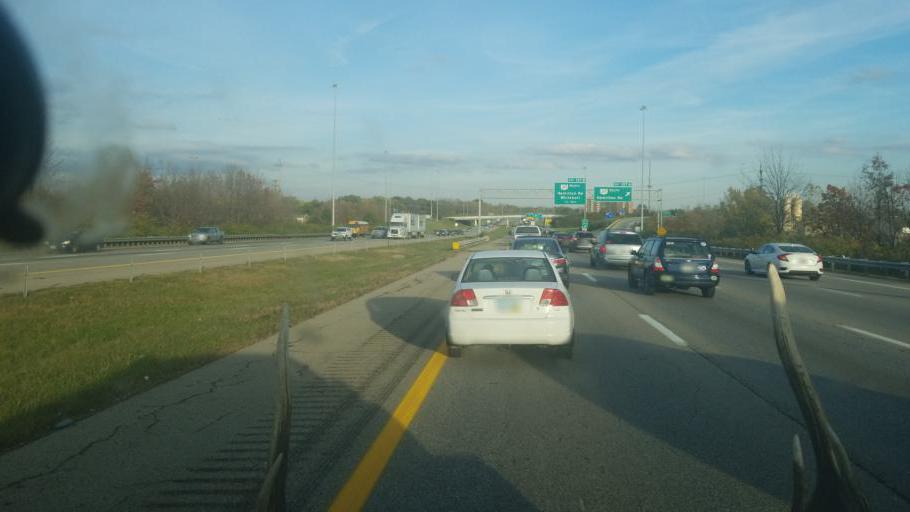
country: US
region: Ohio
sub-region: Franklin County
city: Whitehall
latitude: 39.9361
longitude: -82.8846
